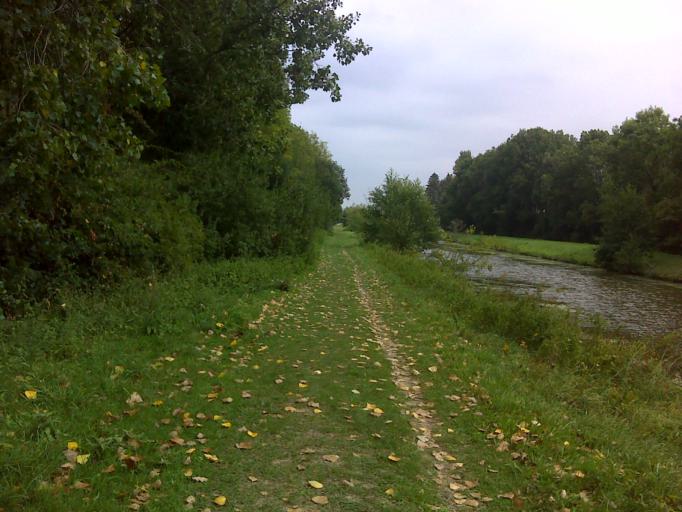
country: FR
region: Nord-Pas-de-Calais
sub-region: Departement du Nord
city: Landrecies
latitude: 50.1230
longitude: 3.6823
